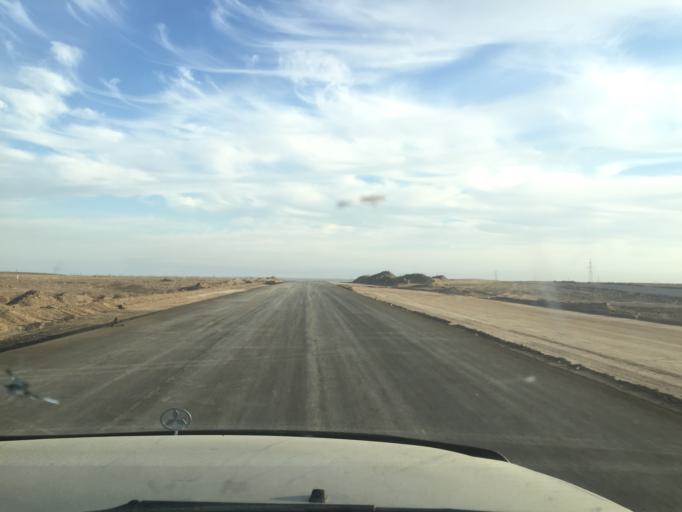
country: KZ
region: Zhambyl
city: Mynaral
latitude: 45.2649
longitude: 73.7960
